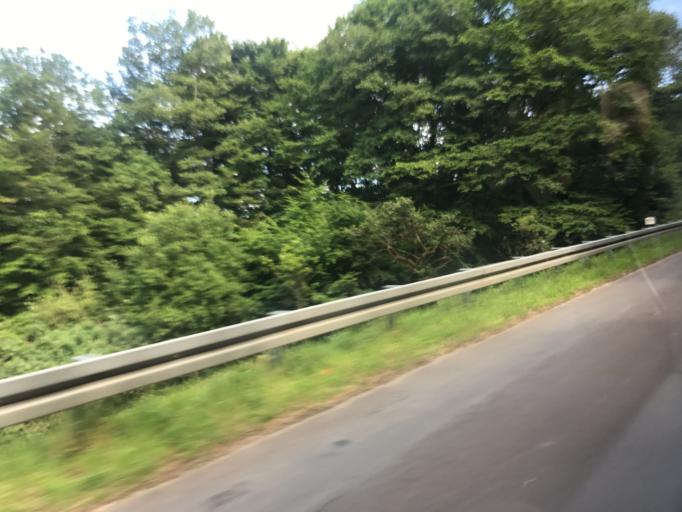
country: DE
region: Hesse
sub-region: Regierungsbezirk Darmstadt
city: Schlangenbad
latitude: 50.0669
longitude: 8.1090
